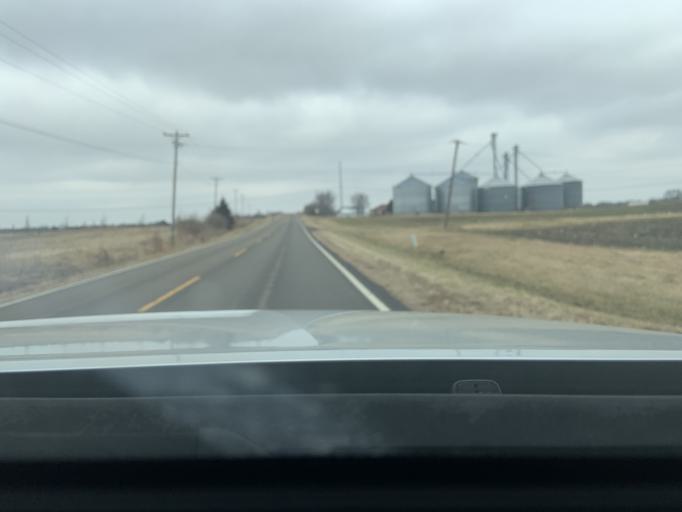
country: US
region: Illinois
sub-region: LaSalle County
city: Seneca
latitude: 41.3725
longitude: -88.6130
